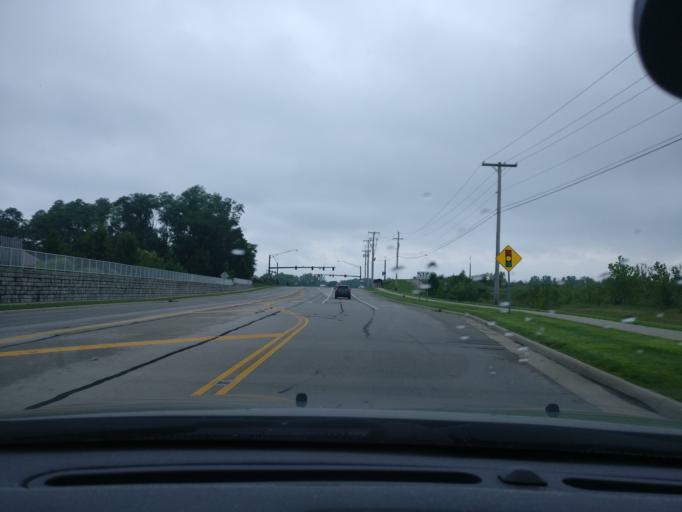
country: US
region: Ohio
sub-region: Warren County
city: Springboro
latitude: 39.5951
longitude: -84.2477
